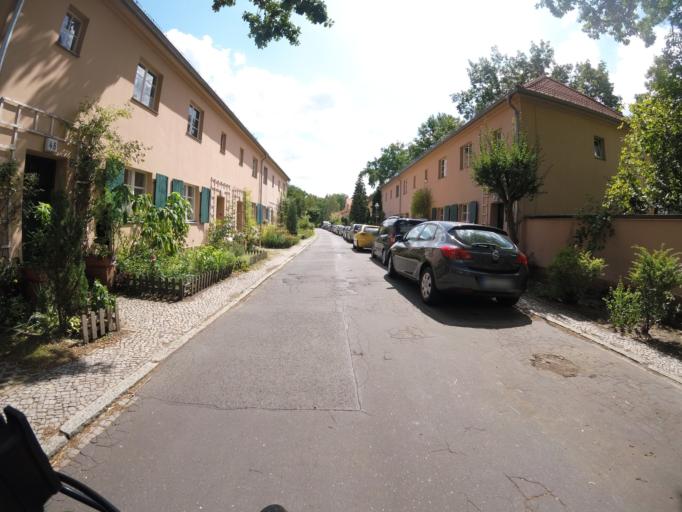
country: DE
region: Berlin
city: Siemensstadt
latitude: 52.5447
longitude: 13.2625
